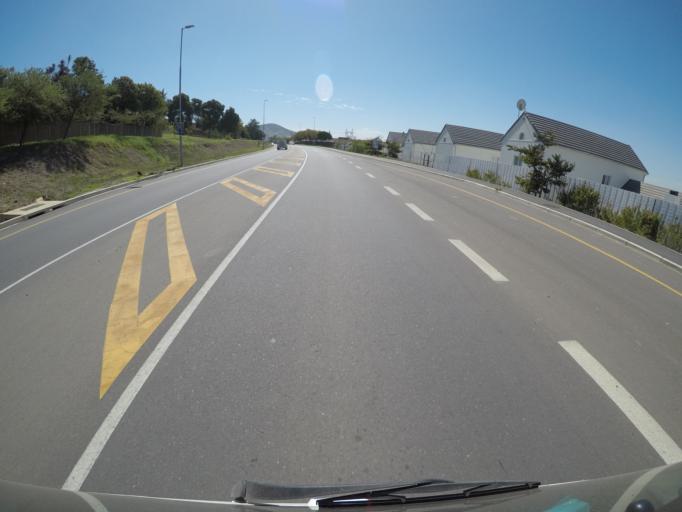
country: ZA
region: Western Cape
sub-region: City of Cape Town
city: Kraaifontein
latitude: -33.8246
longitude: 18.6370
